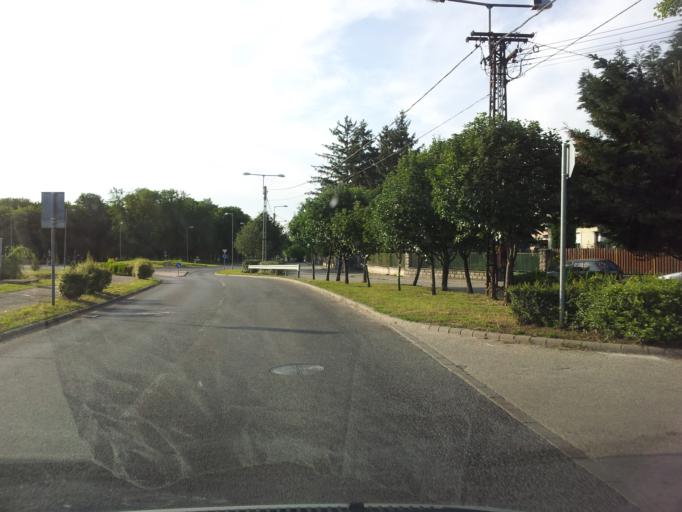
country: HU
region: Komarom-Esztergom
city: Esztergom
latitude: 47.7800
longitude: 18.7511
